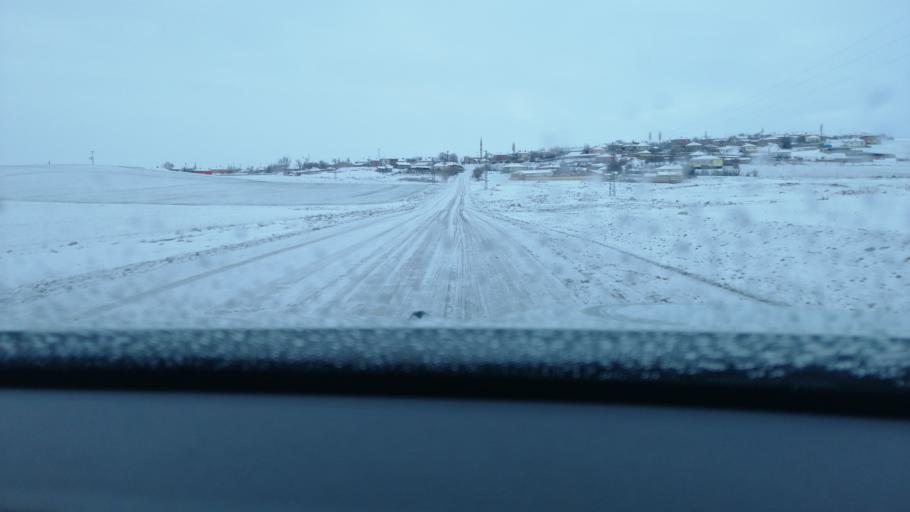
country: TR
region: Aksaray
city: Agacoren
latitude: 38.9402
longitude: 33.9477
